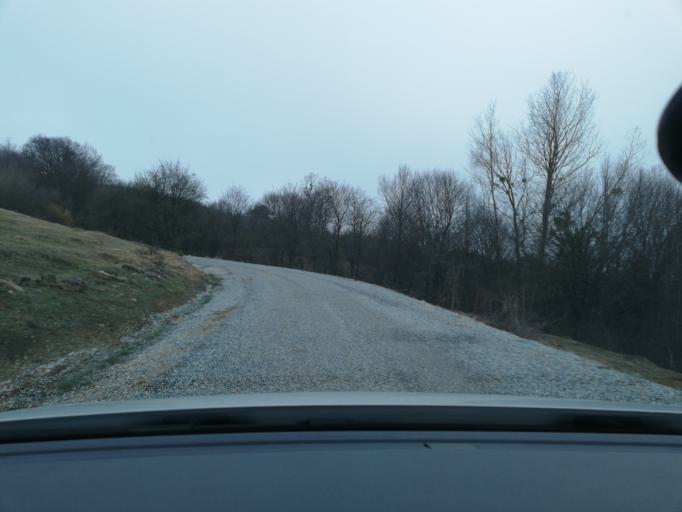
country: TR
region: Bolu
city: Bolu
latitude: 40.6672
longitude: 31.4636
